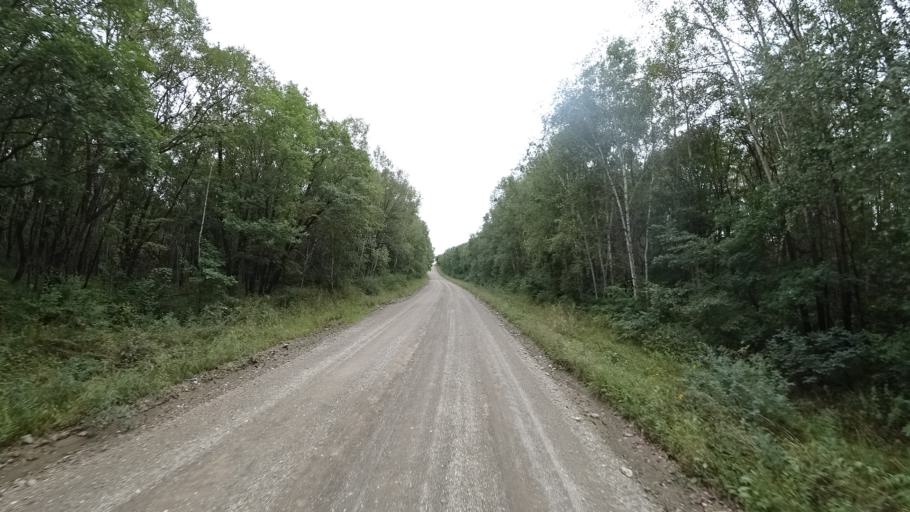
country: RU
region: Primorskiy
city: Ivanovka
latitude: 44.0395
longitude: 132.4965
